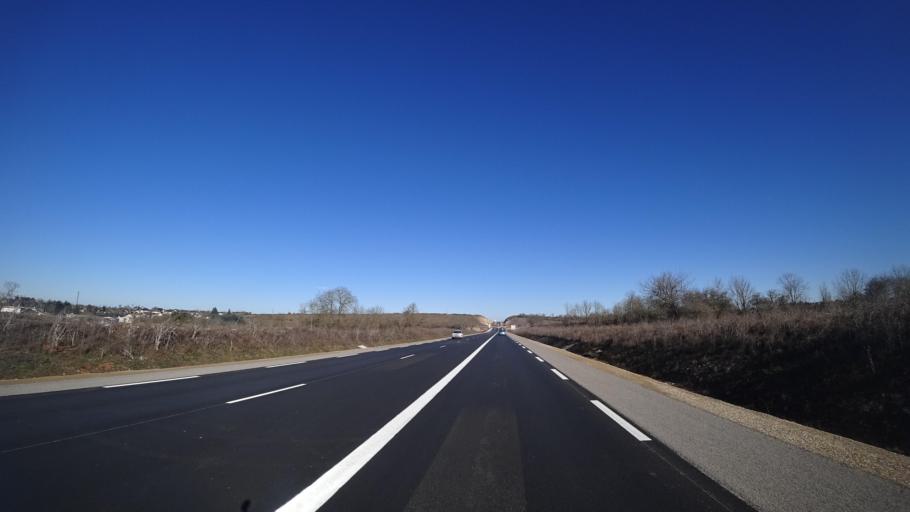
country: FR
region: Midi-Pyrenees
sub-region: Departement de l'Aveyron
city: Sebazac-Concoures
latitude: 44.3962
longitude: 2.6164
